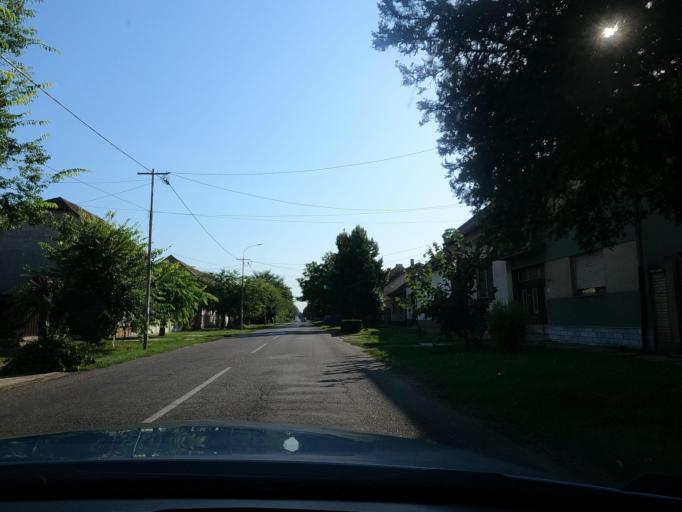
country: RS
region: Autonomna Pokrajina Vojvodina
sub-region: Juznobacki Okrug
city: Becej
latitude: 45.6105
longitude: 20.0421
